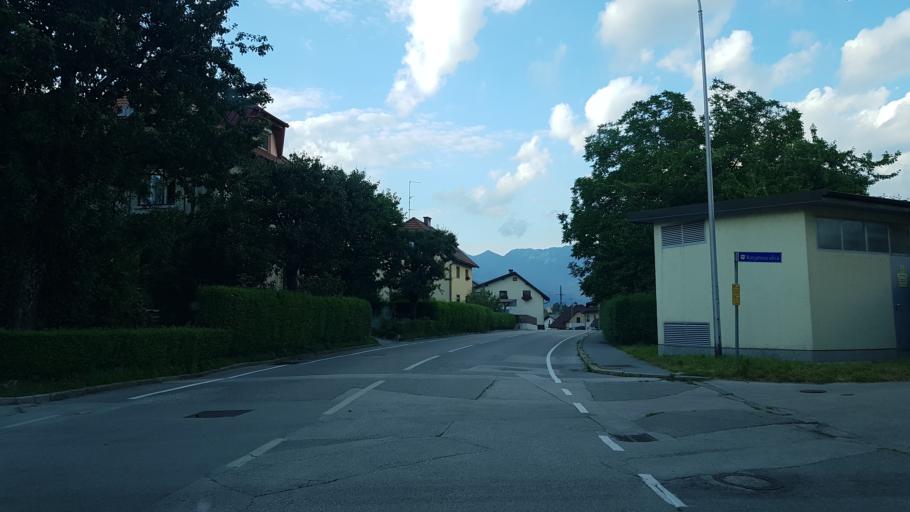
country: SI
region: Kranj
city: Kranj
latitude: 46.2369
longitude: 14.3456
